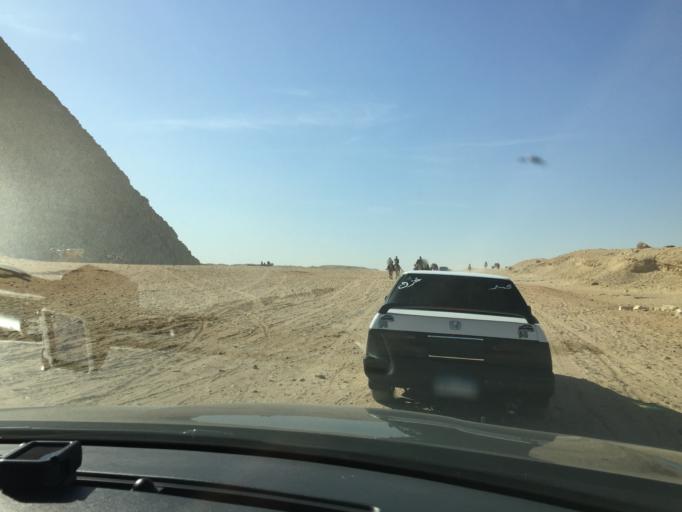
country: EG
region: Al Jizah
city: Al Jizah
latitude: 29.9777
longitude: 31.1326
